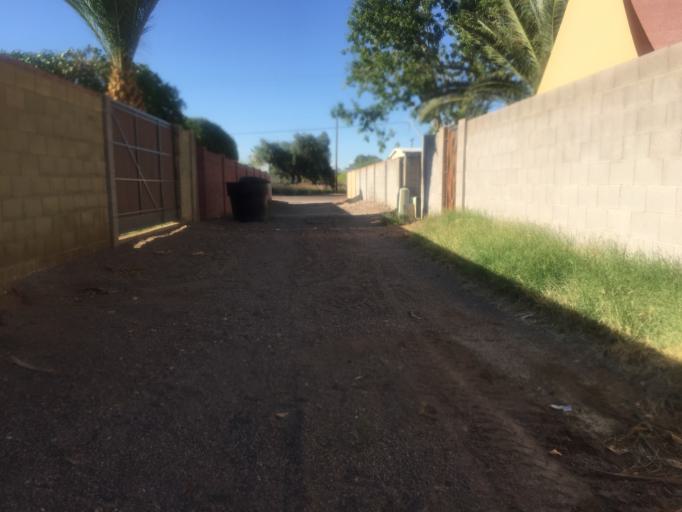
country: US
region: Arizona
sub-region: Maricopa County
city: Paradise Valley
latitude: 33.5748
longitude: -112.0056
